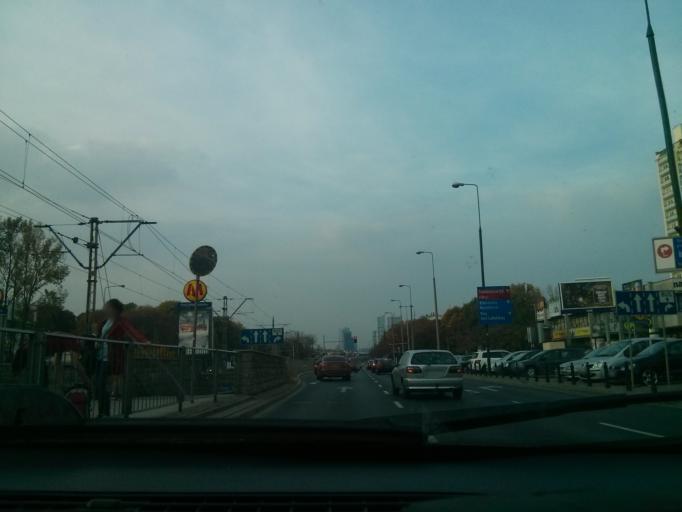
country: PL
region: Masovian Voivodeship
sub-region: Warszawa
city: Warsaw
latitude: 52.2093
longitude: 21.0077
